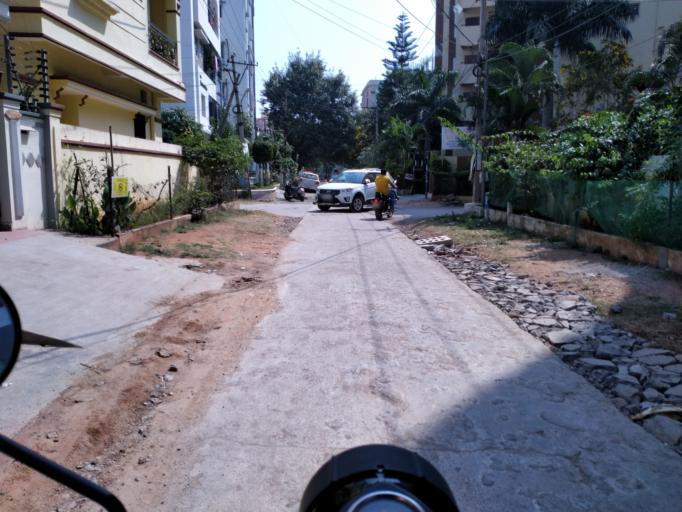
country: IN
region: Telangana
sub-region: Rangareddi
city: Secunderabad
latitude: 17.4960
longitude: 78.5459
